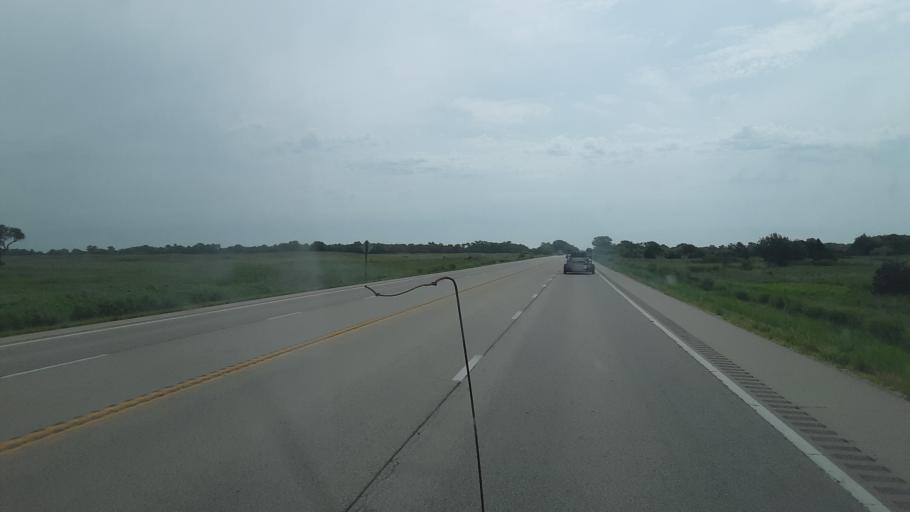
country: US
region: Kansas
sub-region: Rice County
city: Sterling
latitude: 37.9845
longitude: -98.3019
